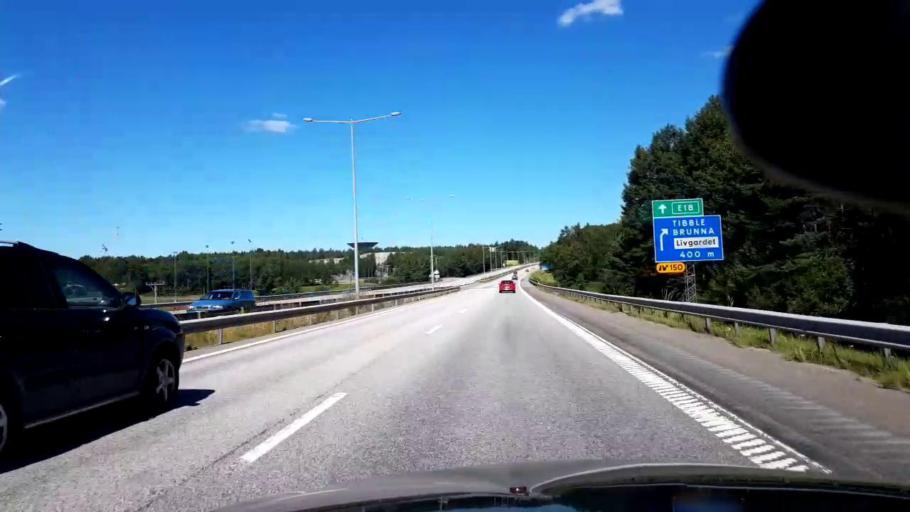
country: SE
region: Stockholm
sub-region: Upplands-Bro Kommun
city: Kungsaengen
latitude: 59.4909
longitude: 17.7510
